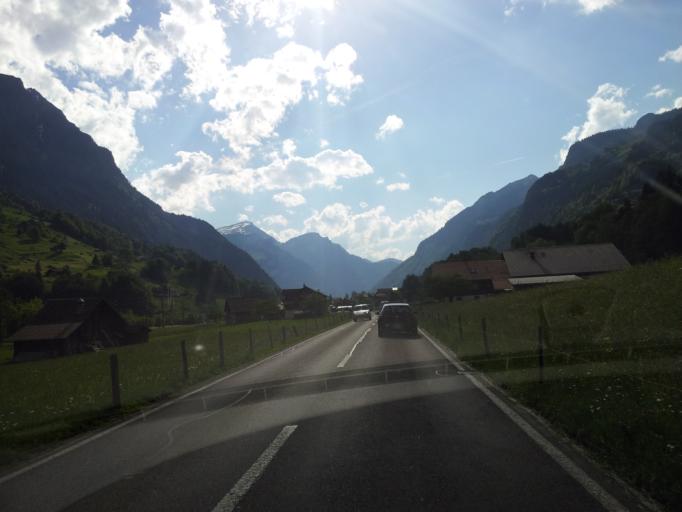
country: CH
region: Bern
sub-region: Interlaken-Oberhasli District
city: Grindelwald
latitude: 46.6364
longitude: 7.9858
